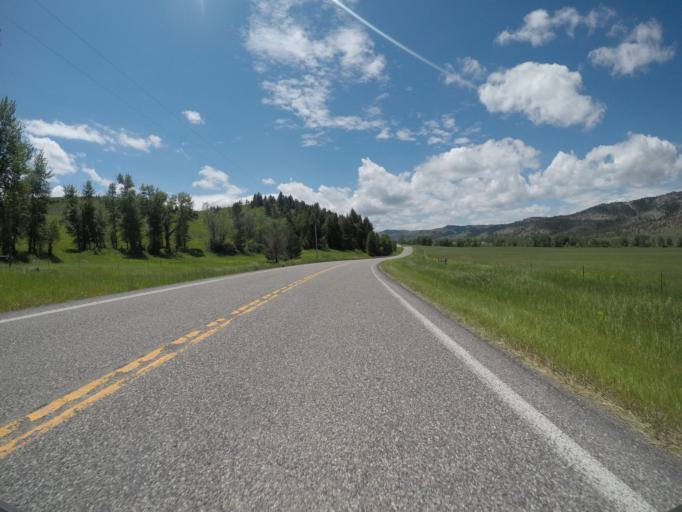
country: US
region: Montana
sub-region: Sweet Grass County
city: Big Timber
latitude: 45.6968
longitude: -110.0238
